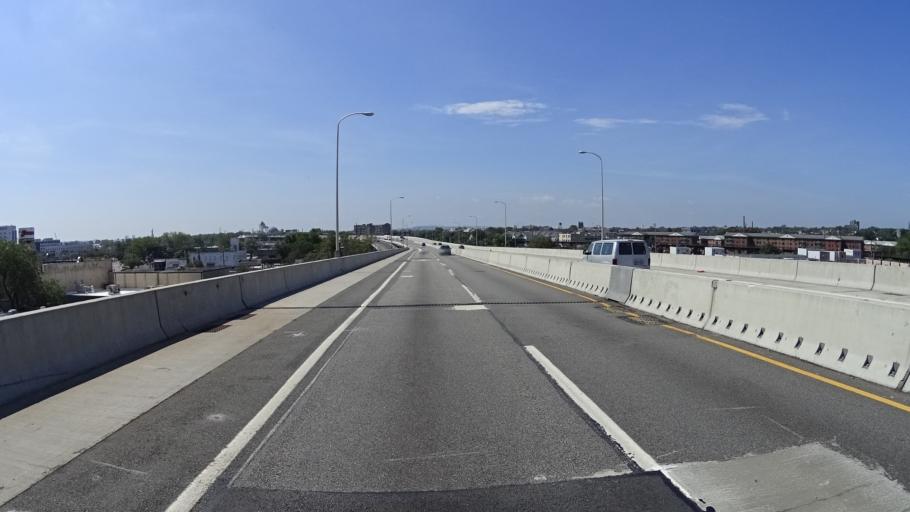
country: US
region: New Jersey
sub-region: Hudson County
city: Jersey City
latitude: 40.7212
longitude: -74.0549
